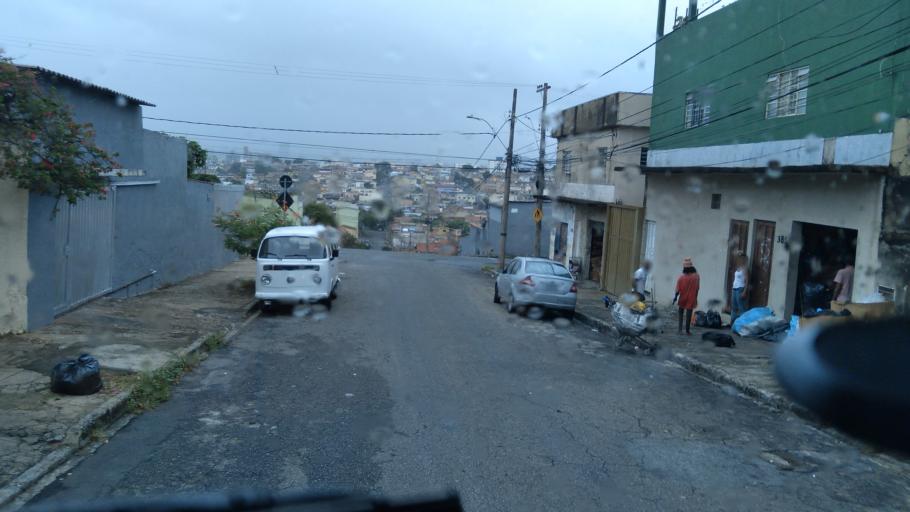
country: BR
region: Minas Gerais
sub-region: Belo Horizonte
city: Belo Horizonte
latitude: -19.9123
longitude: -43.8972
